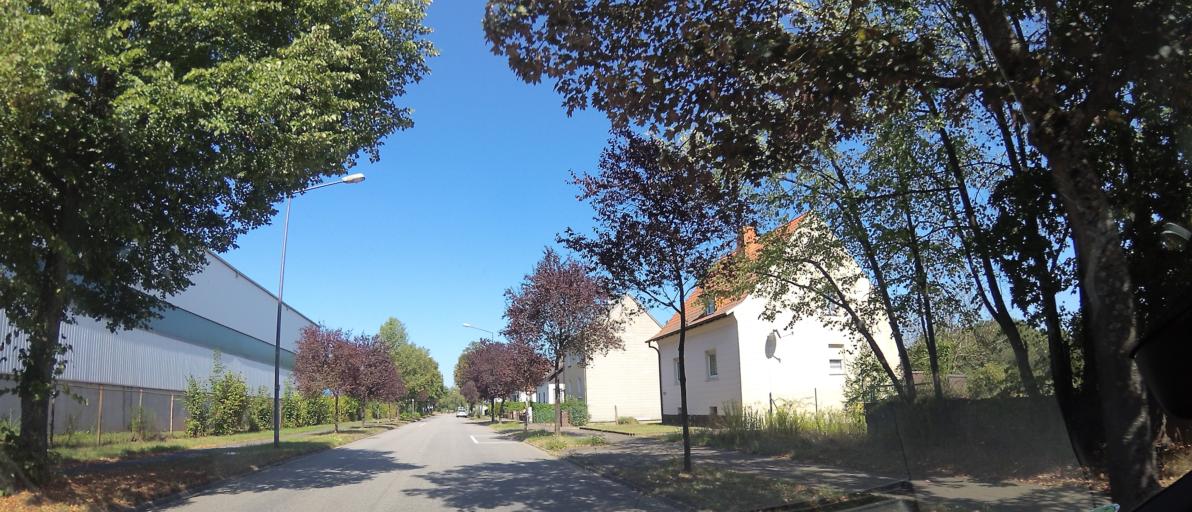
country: DE
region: Saarland
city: Homburg
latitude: 49.3314
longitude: 7.3471
